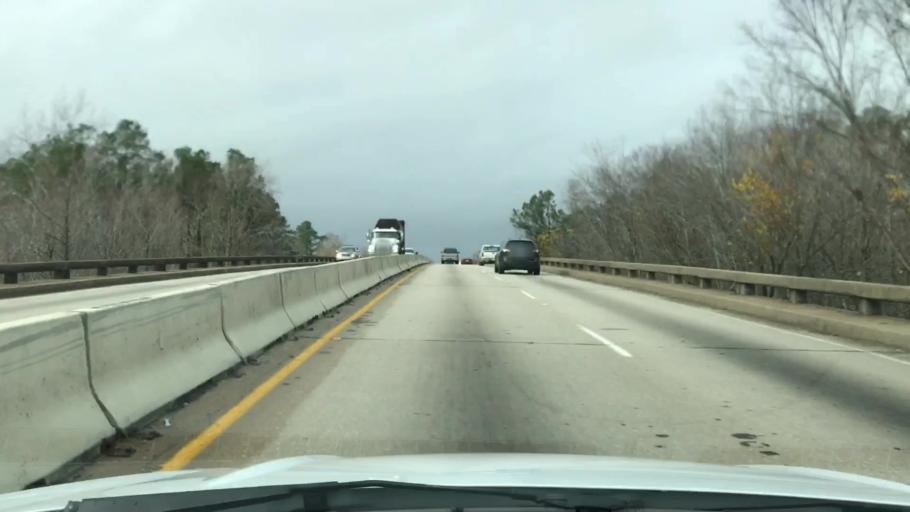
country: US
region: South Carolina
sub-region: Horry County
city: Conway
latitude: 33.8175
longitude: -79.0424
